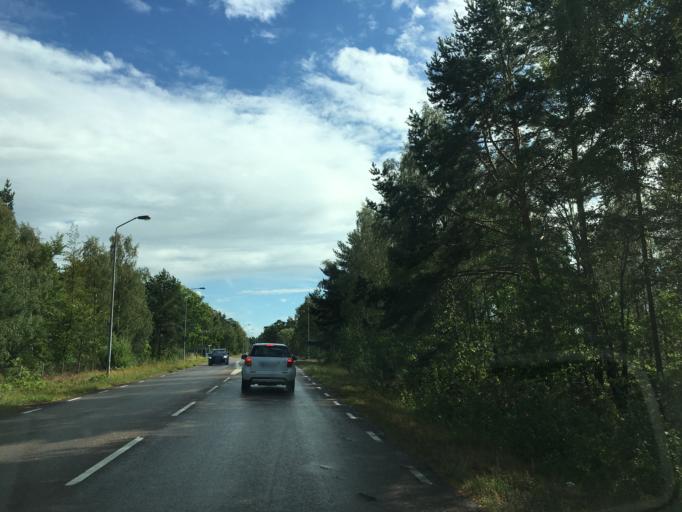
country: SE
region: Kalmar
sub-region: Kalmar Kommun
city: Kalmar
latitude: 56.7044
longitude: 16.3590
